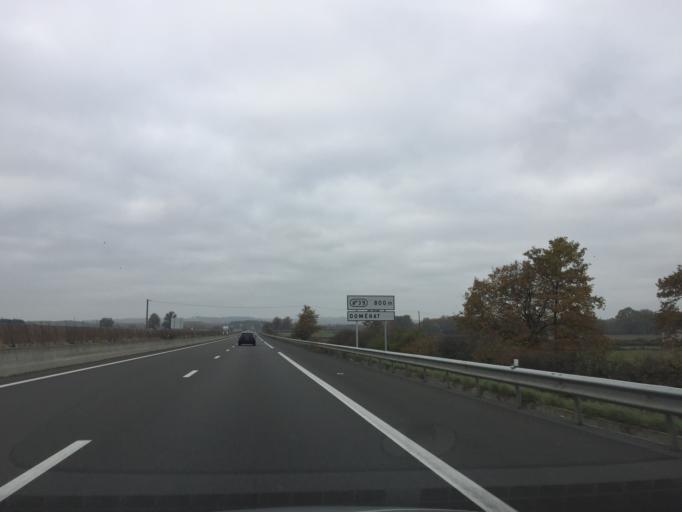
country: FR
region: Auvergne
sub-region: Departement de l'Allier
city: Domerat
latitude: 46.3657
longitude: 2.5596
